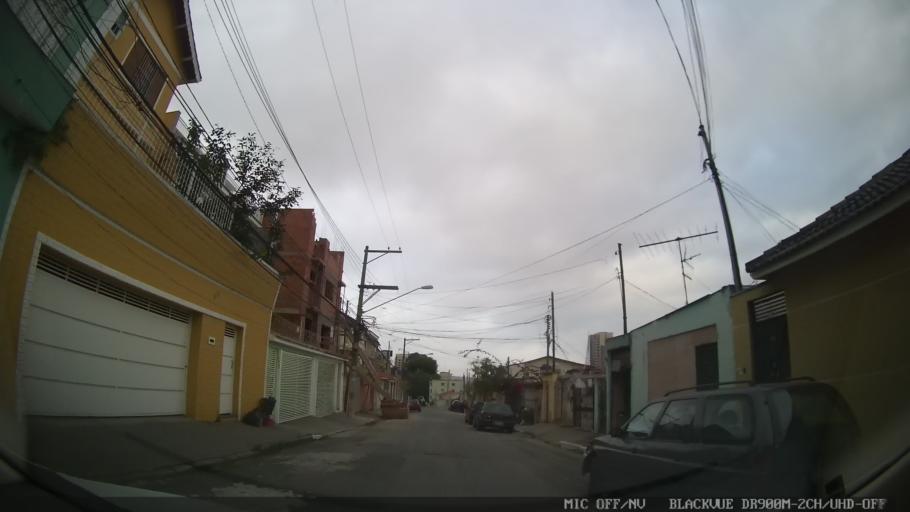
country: BR
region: Sao Paulo
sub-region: Sao Paulo
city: Sao Paulo
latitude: -23.4915
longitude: -46.6236
